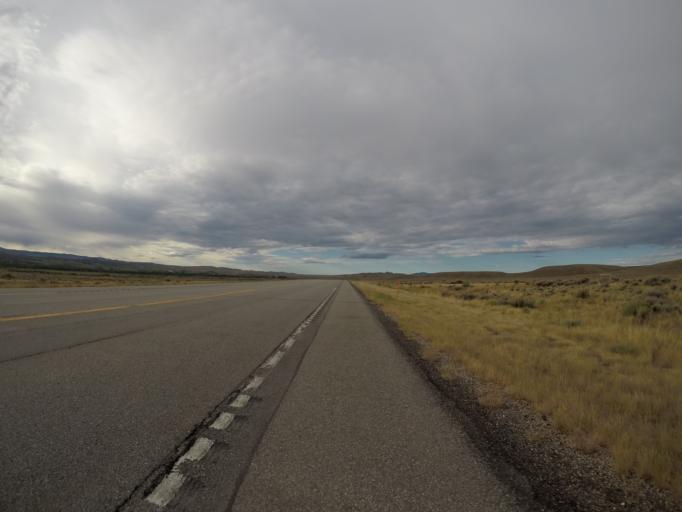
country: US
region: Wyoming
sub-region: Carbon County
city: Saratoga
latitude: 41.3660
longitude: -106.7442
